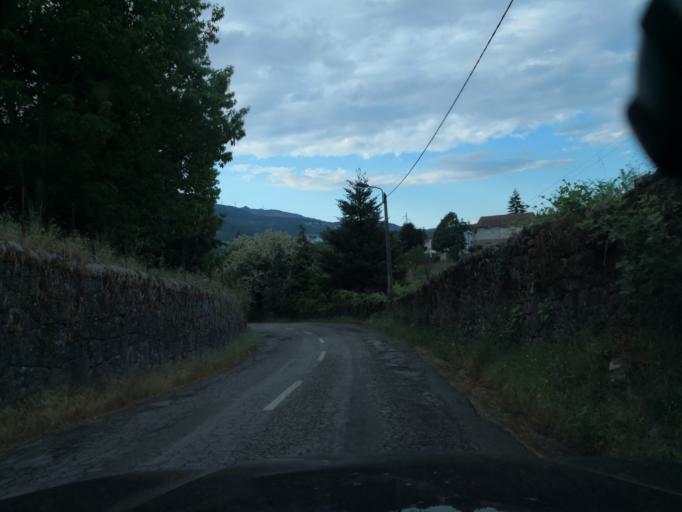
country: PT
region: Vila Real
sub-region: Vila Real
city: Vila Real
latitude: 41.3152
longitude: -7.7426
